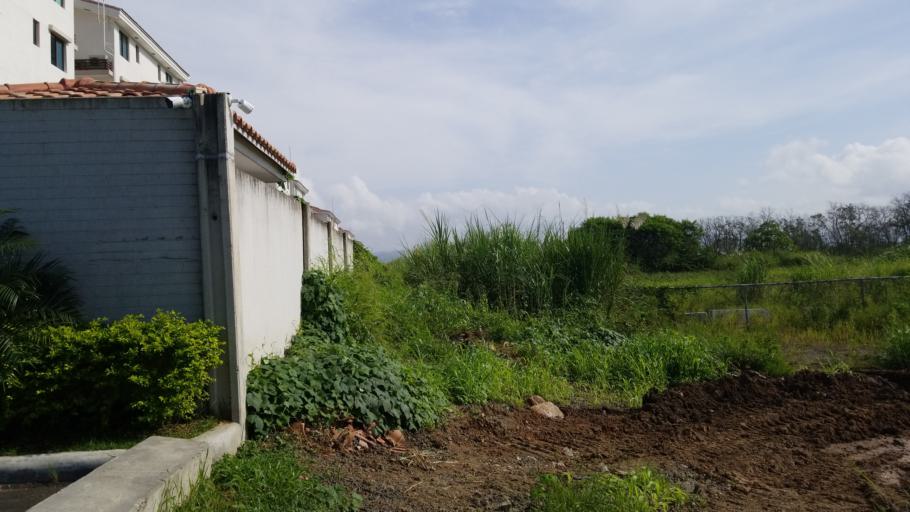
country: PA
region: Panama
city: San Miguelito
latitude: 9.0290
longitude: -79.4157
